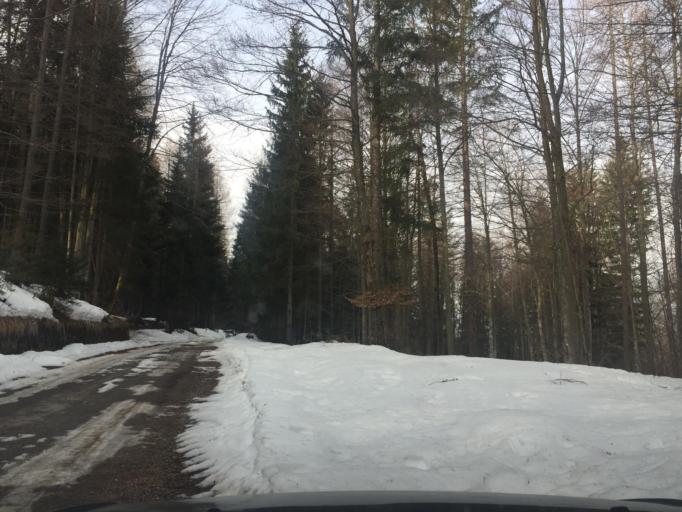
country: AT
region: Carinthia
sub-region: Politischer Bezirk Villach Land
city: Hohenthurn
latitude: 46.5110
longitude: 13.6532
